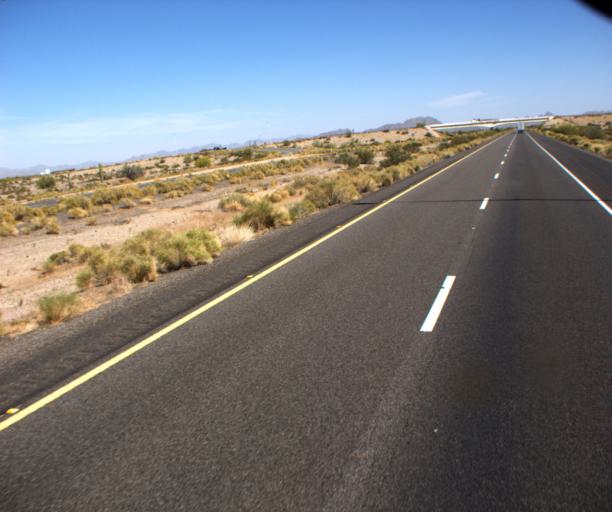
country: US
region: Arizona
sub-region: Maricopa County
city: Gila Bend
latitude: 32.9261
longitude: -112.6758
